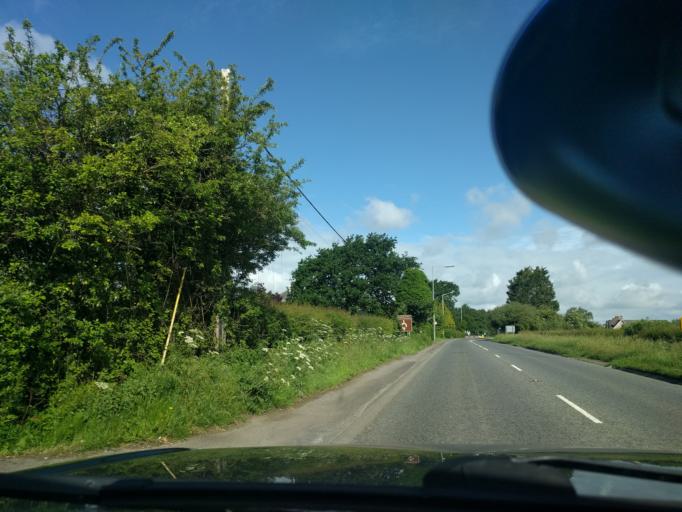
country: GB
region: England
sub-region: Wiltshire
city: Chippenham
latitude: 51.4474
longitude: -2.0896
